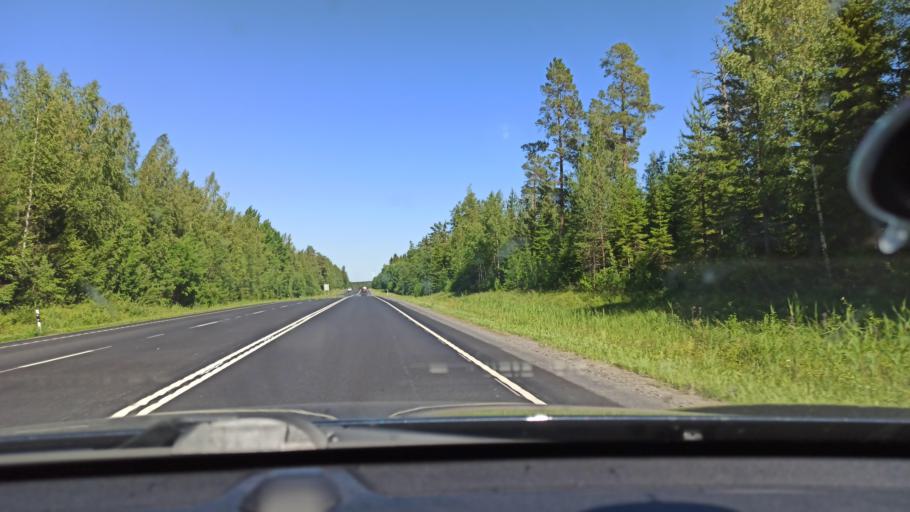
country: FI
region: Ostrobothnia
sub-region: Vaasa
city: Oravais
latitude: 63.2733
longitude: 22.3221
